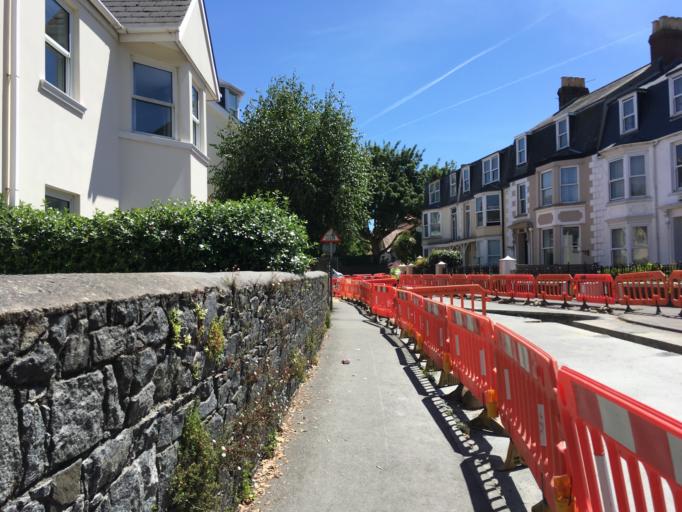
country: GG
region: St Peter Port
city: Saint Peter Port
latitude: 49.4604
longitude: -2.5456
